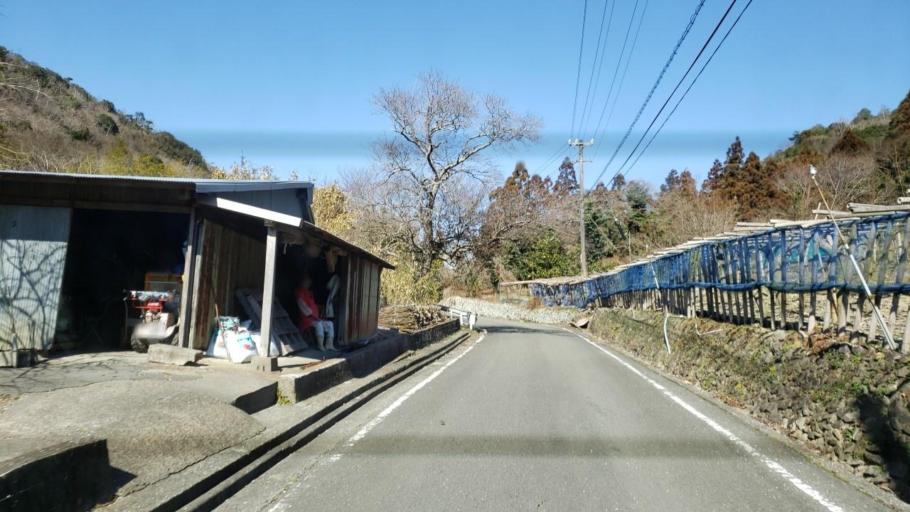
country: JP
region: Tokushima
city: Narutocho-mitsuishi
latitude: 34.1865
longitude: 134.5522
